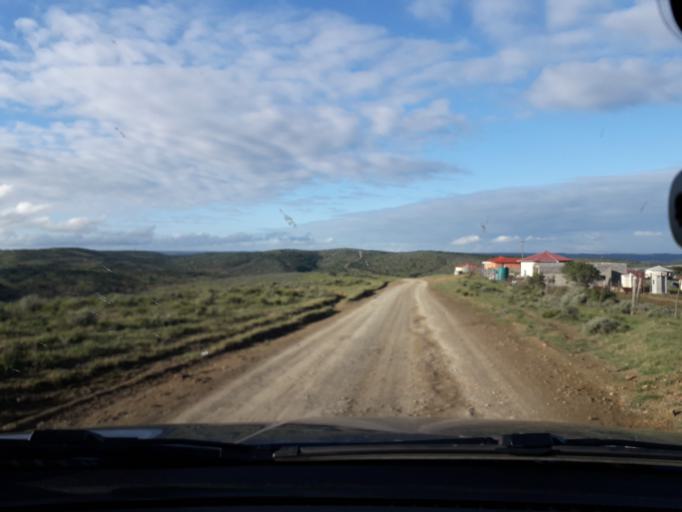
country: ZA
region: Eastern Cape
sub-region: Buffalo City Metropolitan Municipality
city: Bhisho
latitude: -33.1293
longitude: 27.4387
